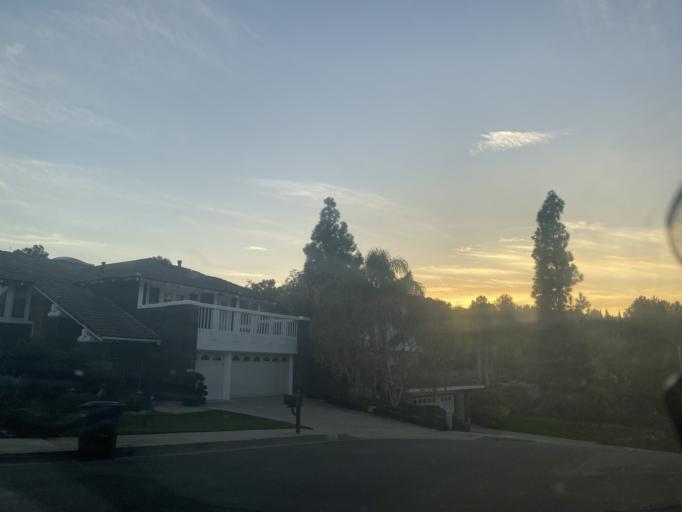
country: US
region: California
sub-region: Orange County
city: North Tustin
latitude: 33.7939
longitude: -117.7763
